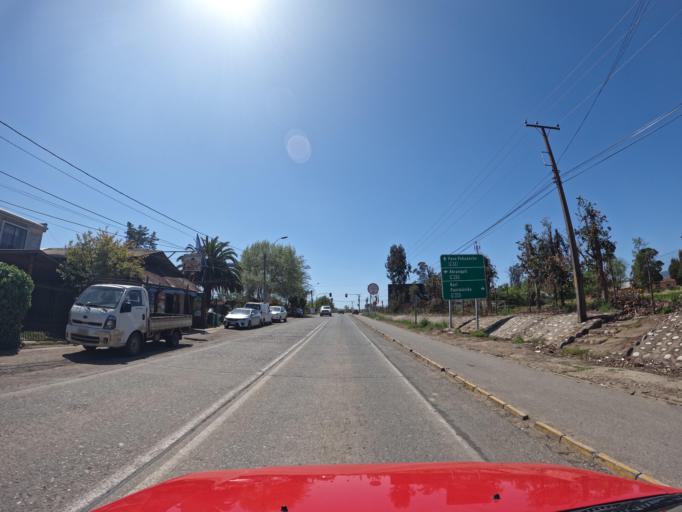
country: CL
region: Maule
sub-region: Provincia de Linares
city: Colbun
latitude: -35.7638
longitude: -71.4217
